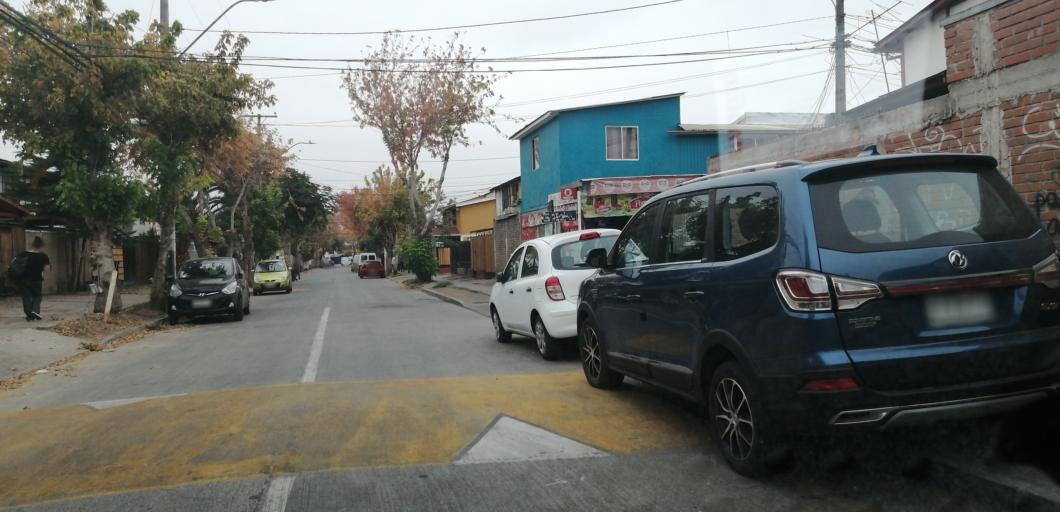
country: CL
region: Santiago Metropolitan
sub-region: Provincia de Santiago
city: Lo Prado
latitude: -33.4554
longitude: -70.7623
